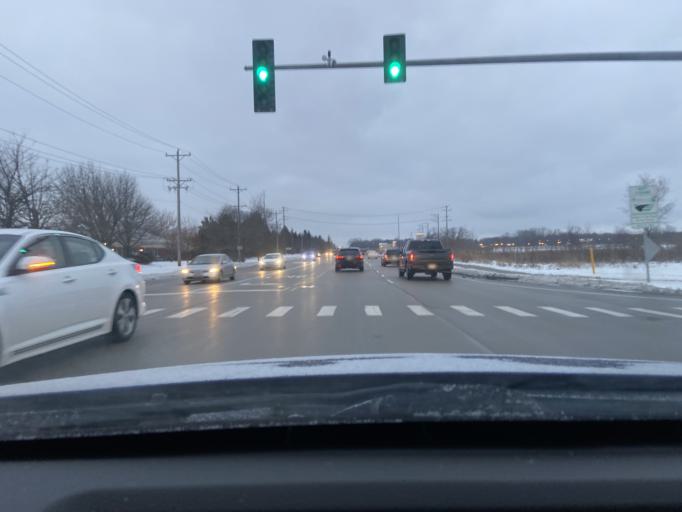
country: US
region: Illinois
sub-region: Lake County
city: Grayslake
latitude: 42.3571
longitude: -88.0438
